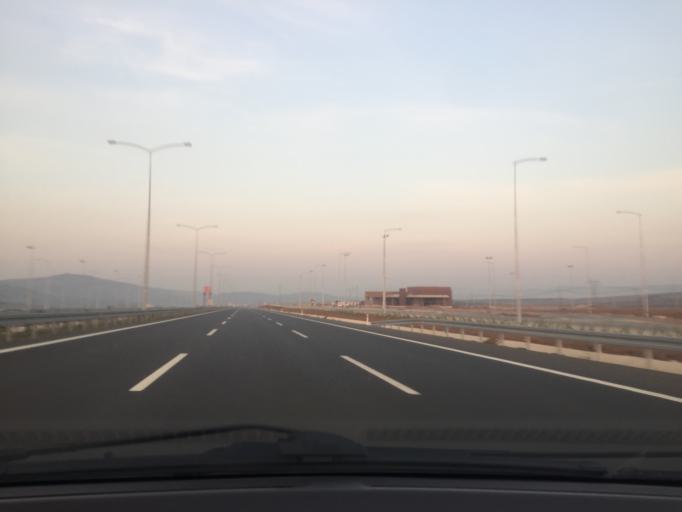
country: TR
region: Bursa
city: Mahmudiye
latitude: 40.2727
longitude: 28.6031
